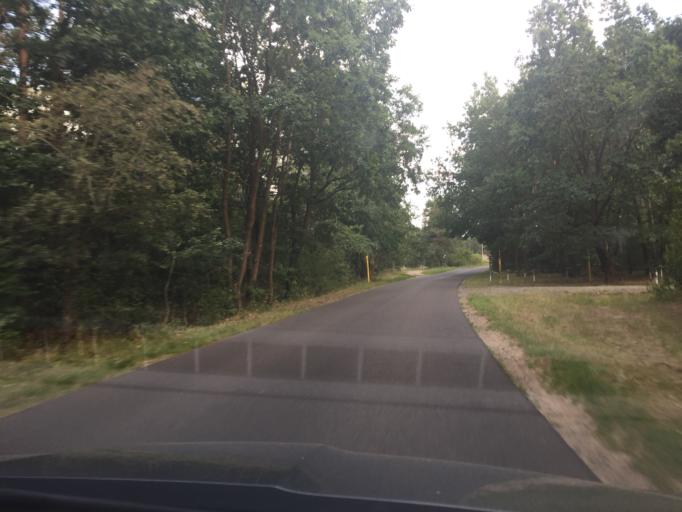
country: DE
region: Brandenburg
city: Erkner
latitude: 52.3792
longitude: 13.7718
